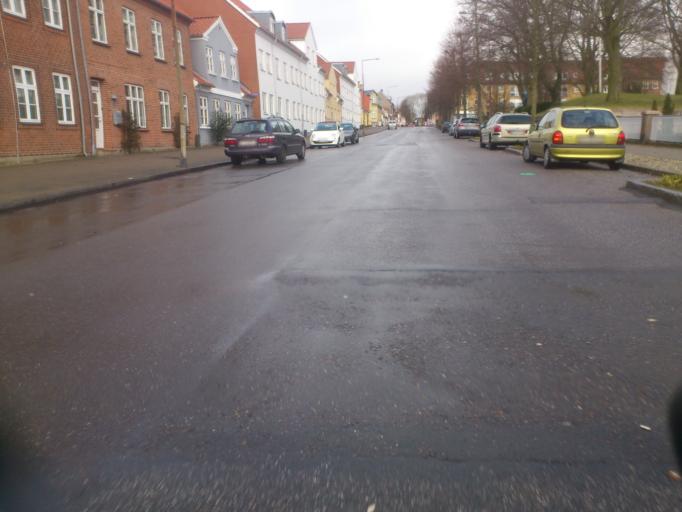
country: DK
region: South Denmark
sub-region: Fredericia Kommune
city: Fredericia
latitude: 55.5659
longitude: 9.7637
